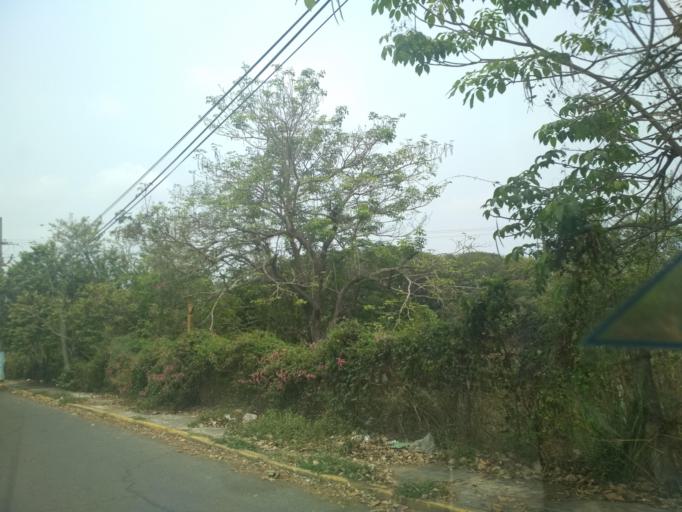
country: MX
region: Veracruz
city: El Tejar
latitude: 19.0568
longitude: -96.1612
